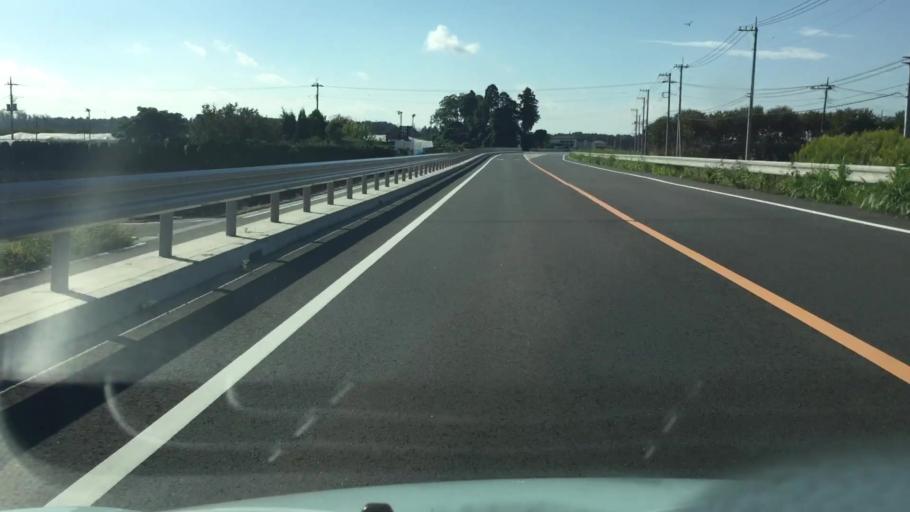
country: JP
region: Tochigi
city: Ujiie
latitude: 36.5949
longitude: 139.9851
